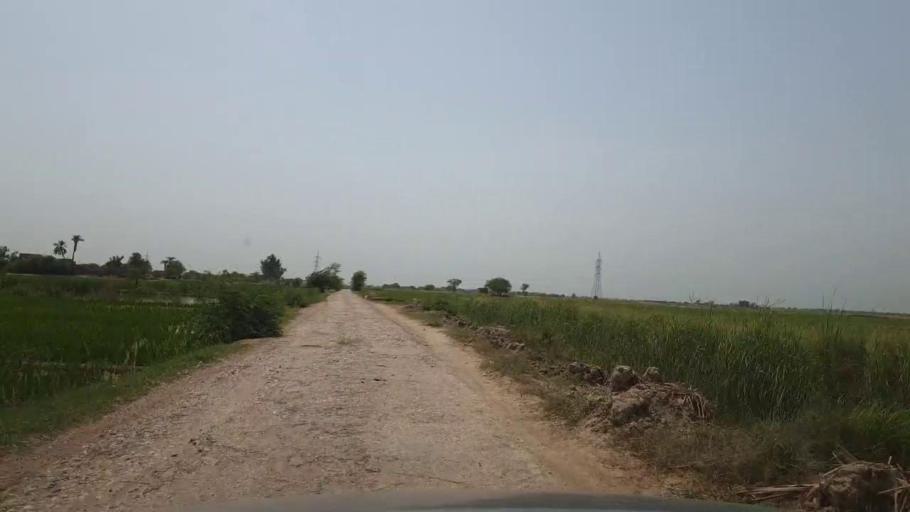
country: PK
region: Sindh
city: Garhi Yasin
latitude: 27.8959
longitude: 68.4839
